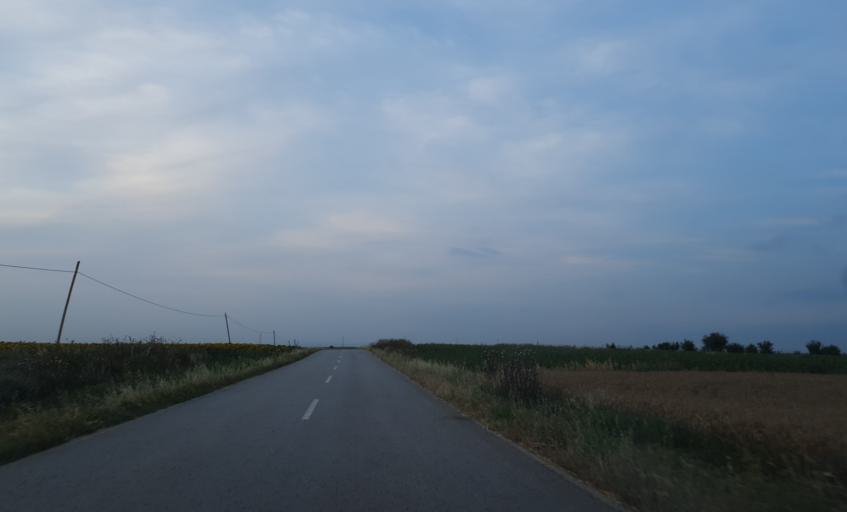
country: TR
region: Kirklareli
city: Buyukkaristiran
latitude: 41.3213
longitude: 27.6058
